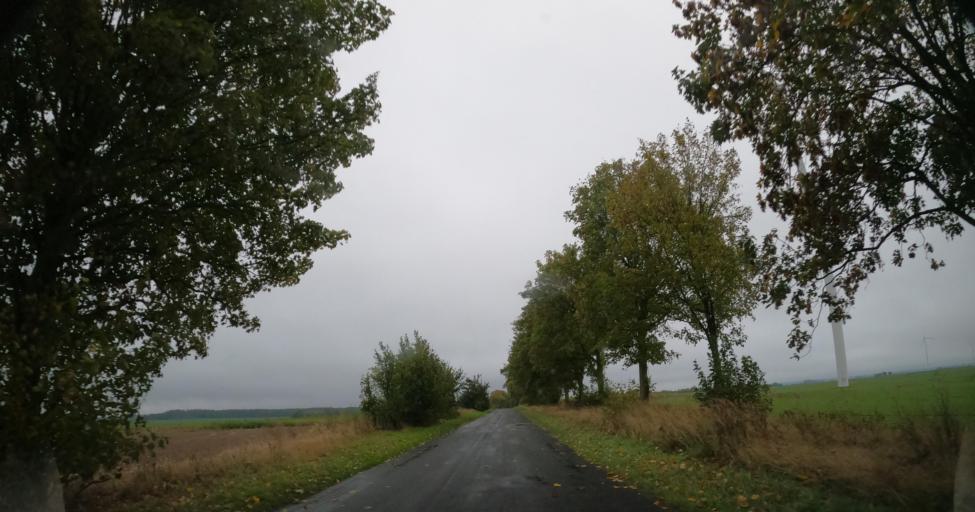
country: PL
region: West Pomeranian Voivodeship
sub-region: Powiat pyrzycki
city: Kozielice
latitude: 53.0786
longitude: 14.7807
